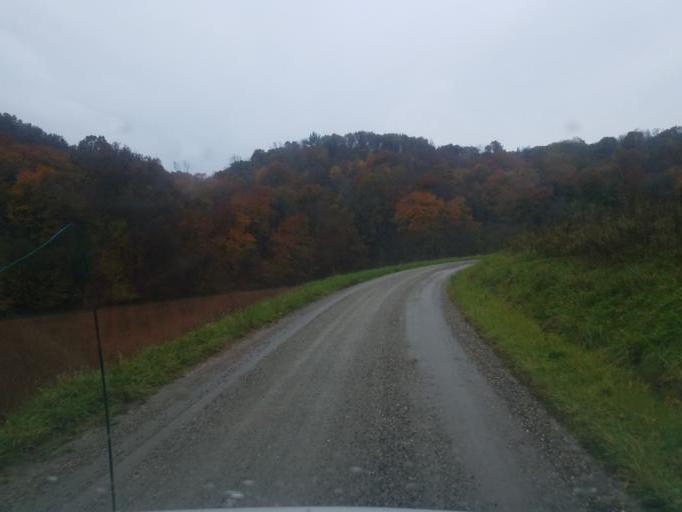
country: US
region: Ohio
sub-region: Washington County
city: Beverly
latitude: 39.4710
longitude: -81.7489
